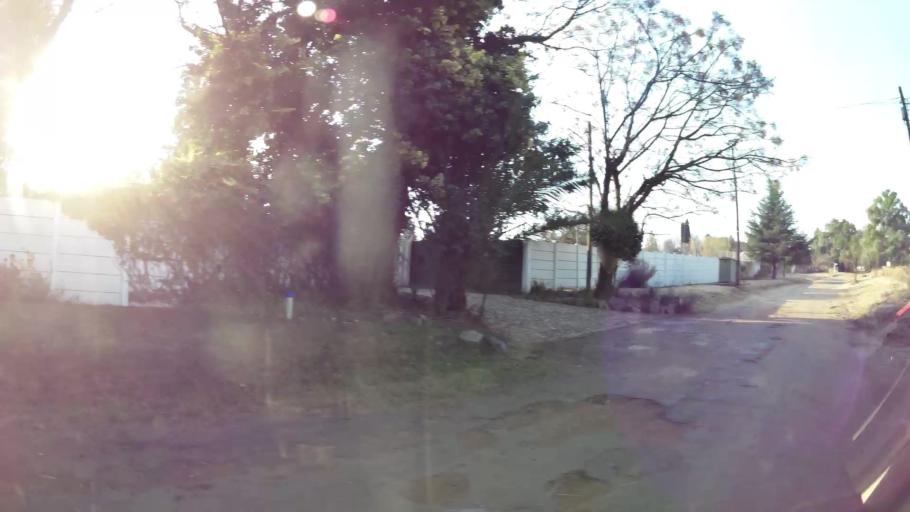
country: ZA
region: Gauteng
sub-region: Ekurhuleni Metropolitan Municipality
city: Benoni
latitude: -26.1549
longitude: 28.3668
